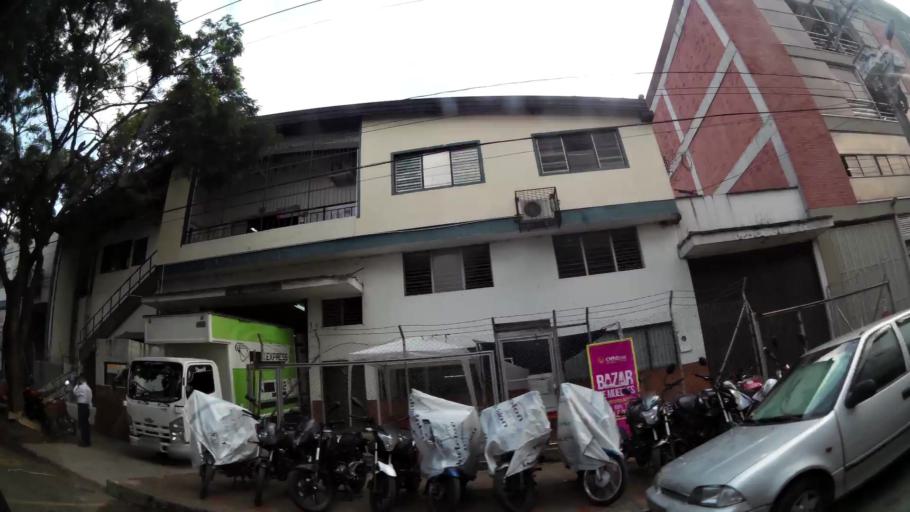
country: CO
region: Antioquia
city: Itagui
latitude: 6.2167
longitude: -75.5823
